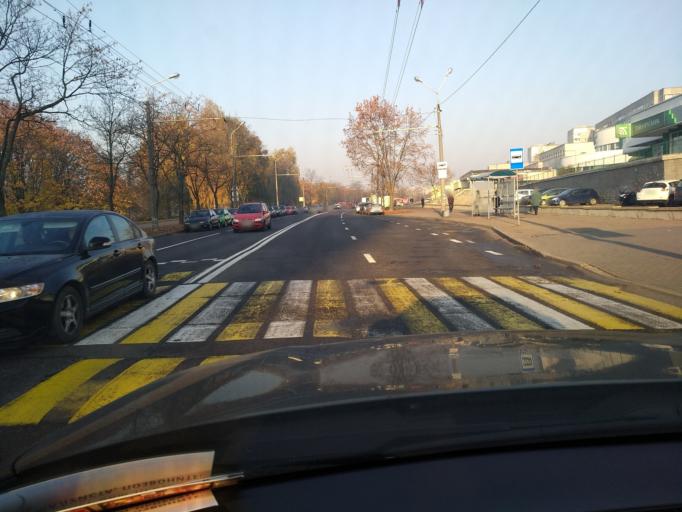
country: BY
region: Minsk
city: Borovlyany
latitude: 53.9506
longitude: 27.6377
